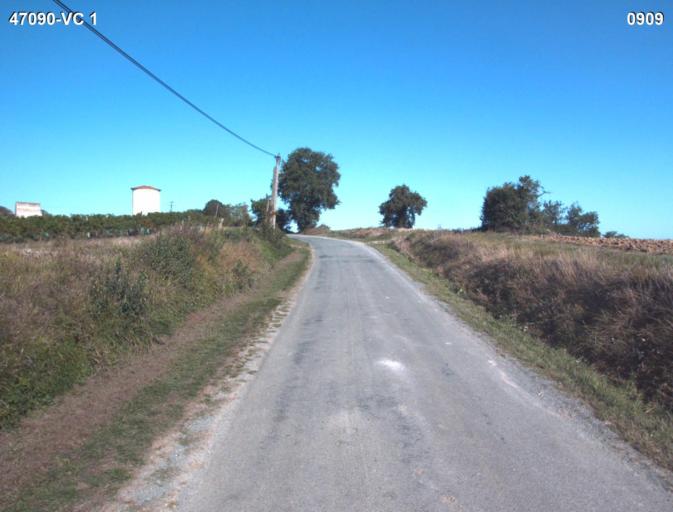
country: FR
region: Aquitaine
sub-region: Departement du Lot-et-Garonne
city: Nerac
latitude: 44.1667
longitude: 0.3813
